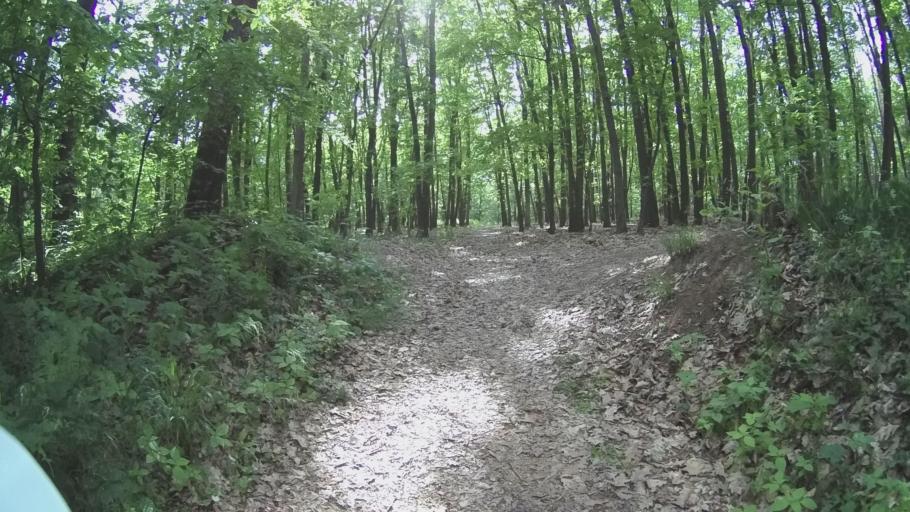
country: CZ
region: Central Bohemia
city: Zdiby
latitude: 50.2055
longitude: 14.4472
